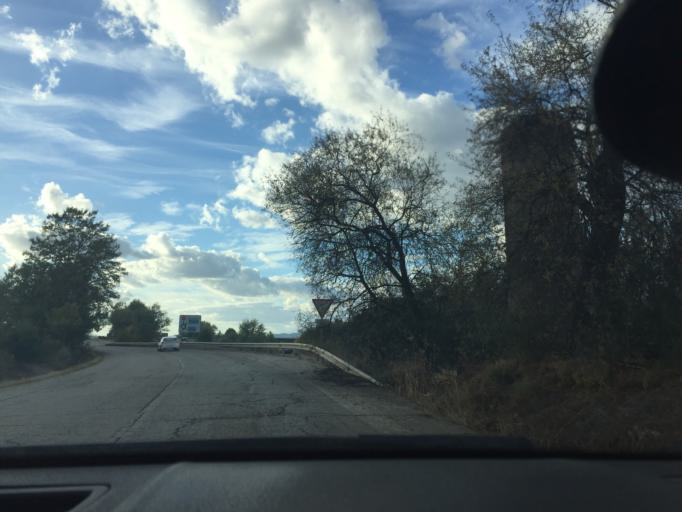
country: ES
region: Andalusia
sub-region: Province of Cordoba
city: El Carpio
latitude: 37.9510
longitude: -4.5096
